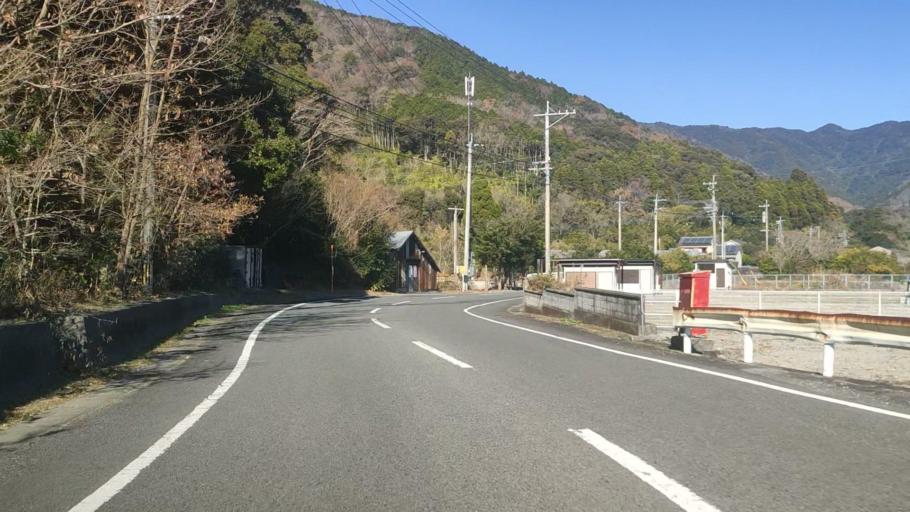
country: JP
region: Oita
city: Saiki
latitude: 32.8006
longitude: 131.8884
